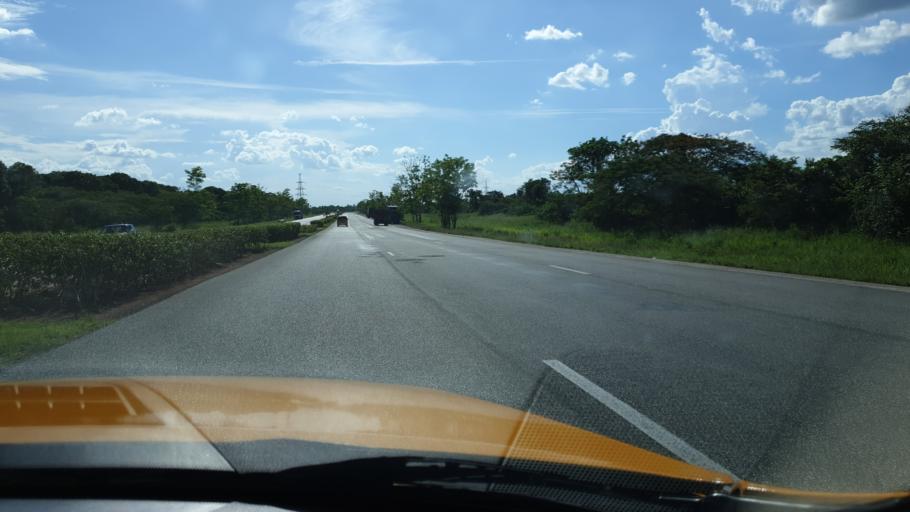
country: CU
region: Cienfuegos
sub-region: Municipio de Aguada de Pasajeros
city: Aguada de Pasajeros
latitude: 22.4075
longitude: -80.8799
